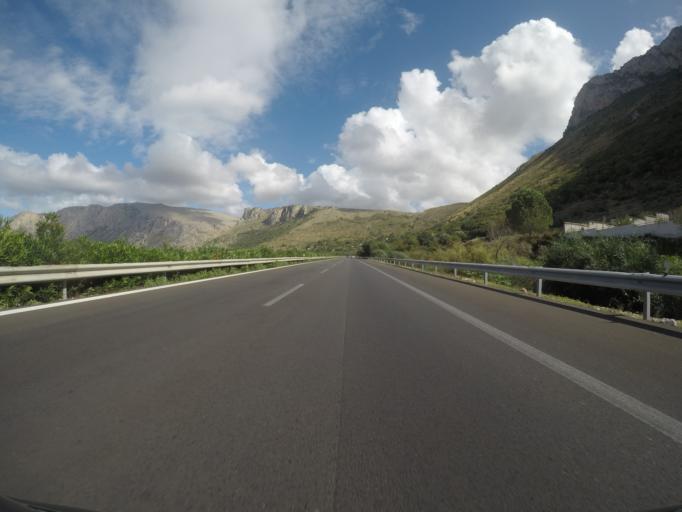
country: IT
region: Sicily
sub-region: Palermo
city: Terrasini
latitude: 38.1357
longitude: 13.0873
